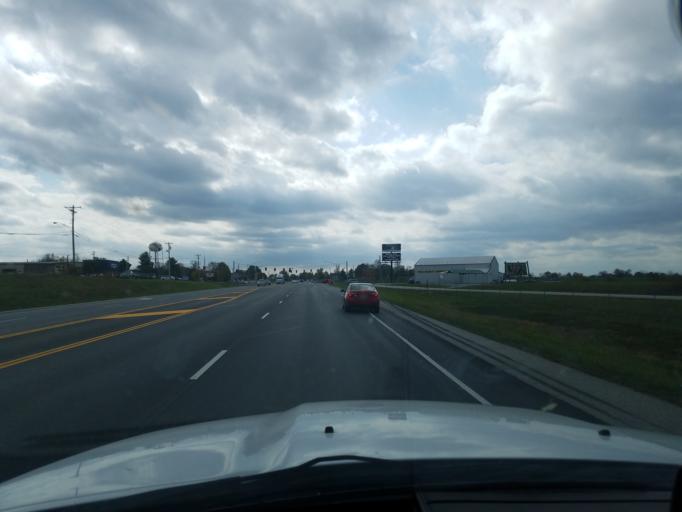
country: US
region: Kentucky
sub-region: Marion County
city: Lebanon
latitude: 37.5931
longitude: -85.2507
